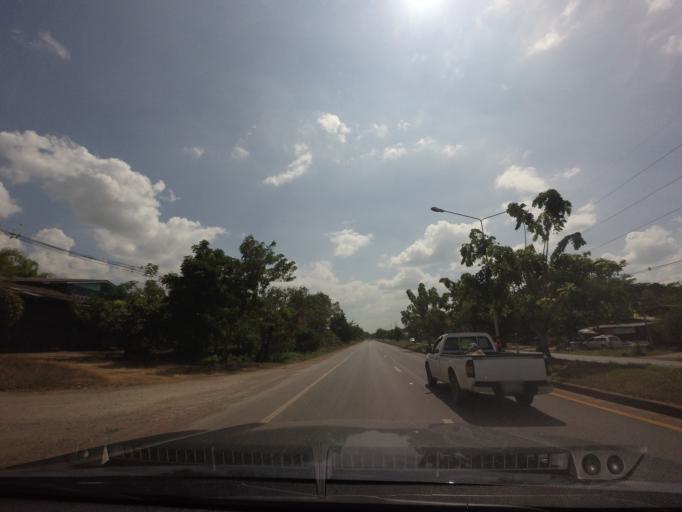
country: TH
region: Phetchabun
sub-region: Amphoe Bueng Sam Phan
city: Bueng Sam Phan
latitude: 15.8785
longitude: 101.0174
